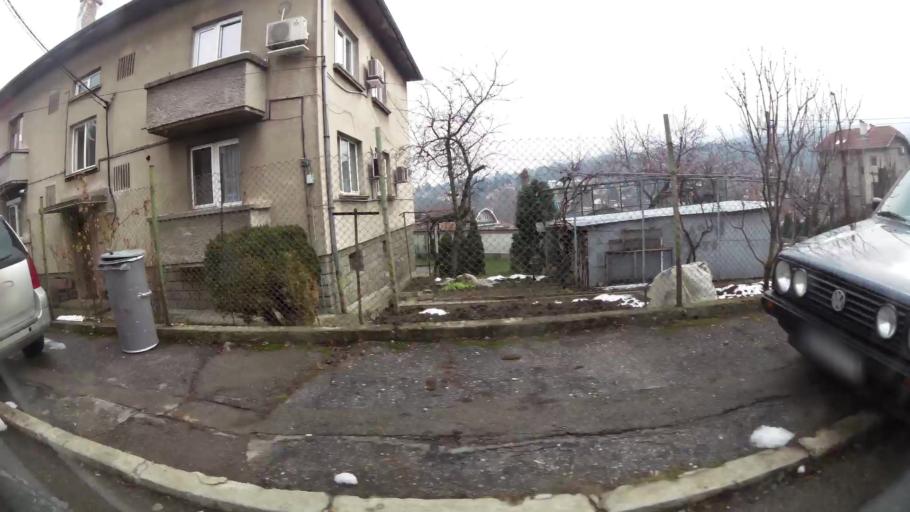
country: BG
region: Sofia-Capital
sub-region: Stolichna Obshtina
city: Sofia
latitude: 42.6615
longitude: 23.2410
